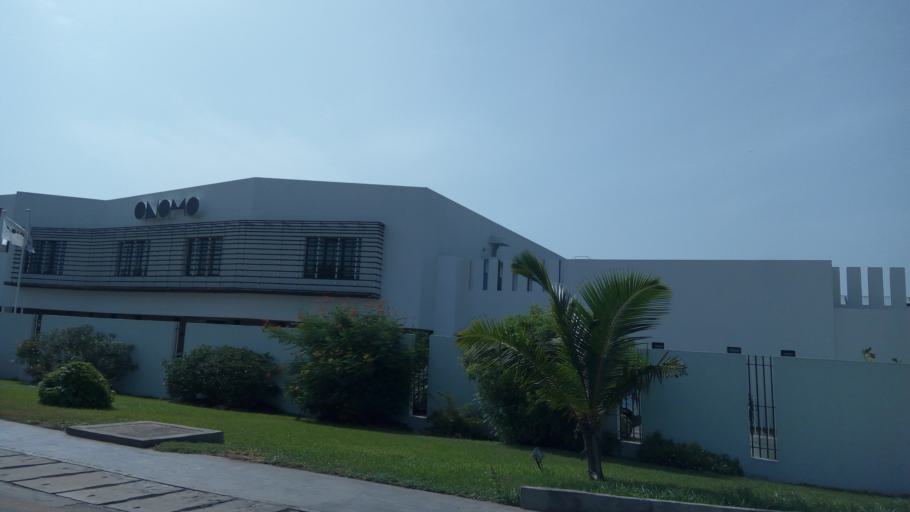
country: TG
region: Maritime
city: Lome
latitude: 6.1303
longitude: 1.2447
